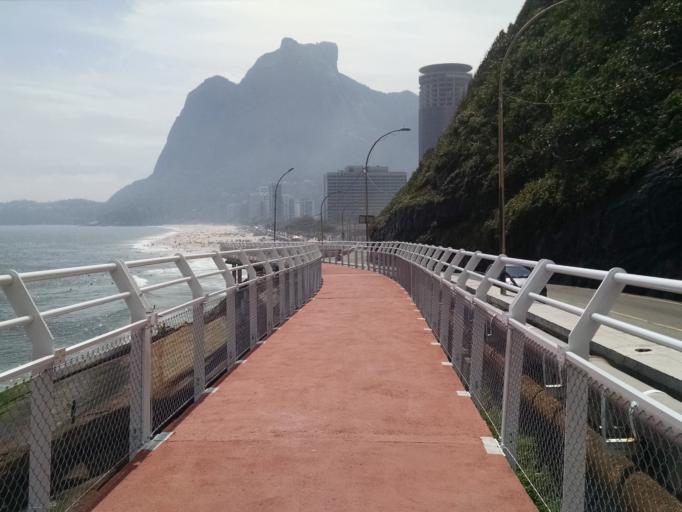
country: BR
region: Rio de Janeiro
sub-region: Rio De Janeiro
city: Rio de Janeiro
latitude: -22.9986
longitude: -43.2527
